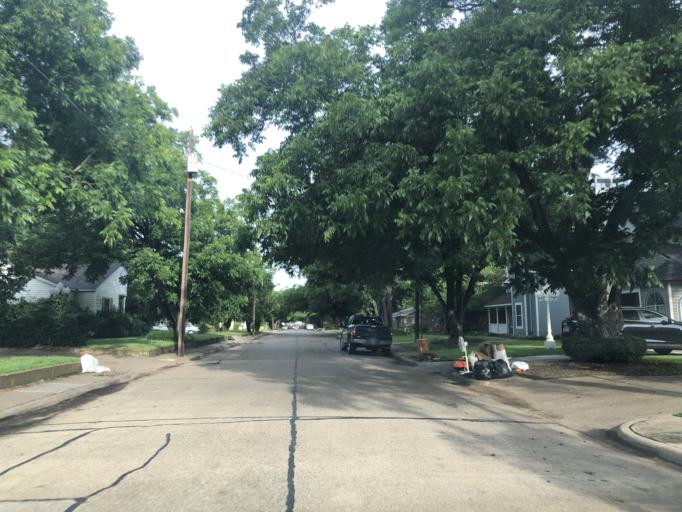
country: US
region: Texas
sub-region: Dallas County
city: Irving
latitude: 32.8035
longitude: -96.9786
